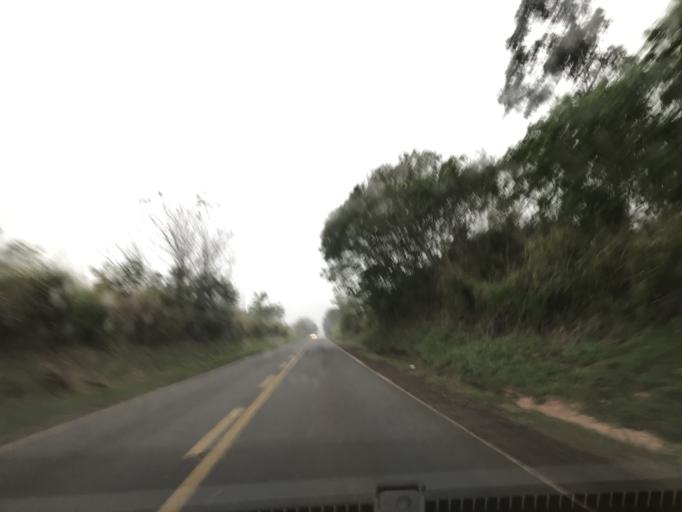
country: PY
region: Canindeyu
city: Salto del Guaira
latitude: -24.1048
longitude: -54.1058
